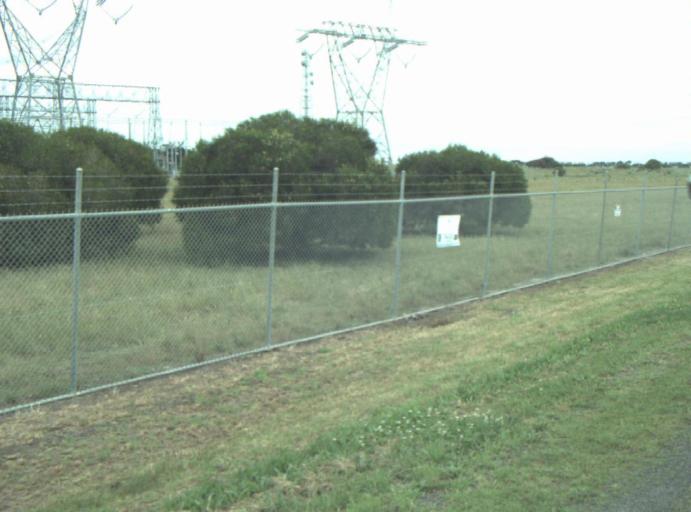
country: AU
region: Victoria
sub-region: Greater Geelong
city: Bell Post Hill
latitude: -38.0357
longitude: 144.3005
